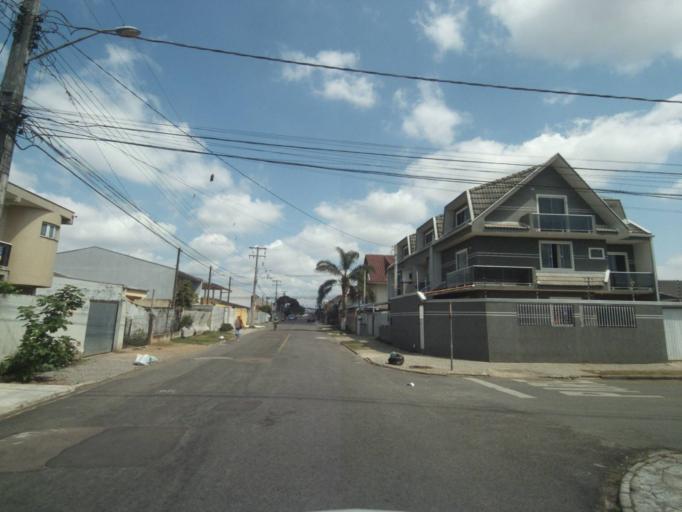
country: BR
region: Parana
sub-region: Sao Jose Dos Pinhais
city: Sao Jose dos Pinhais
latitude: -25.5399
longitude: -49.2649
